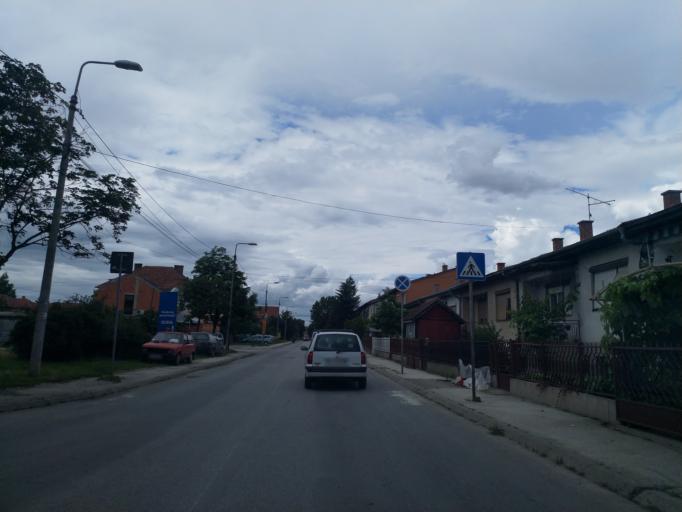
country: RS
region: Central Serbia
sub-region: Pomoravski Okrug
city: Jagodina
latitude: 43.9723
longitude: 21.2739
